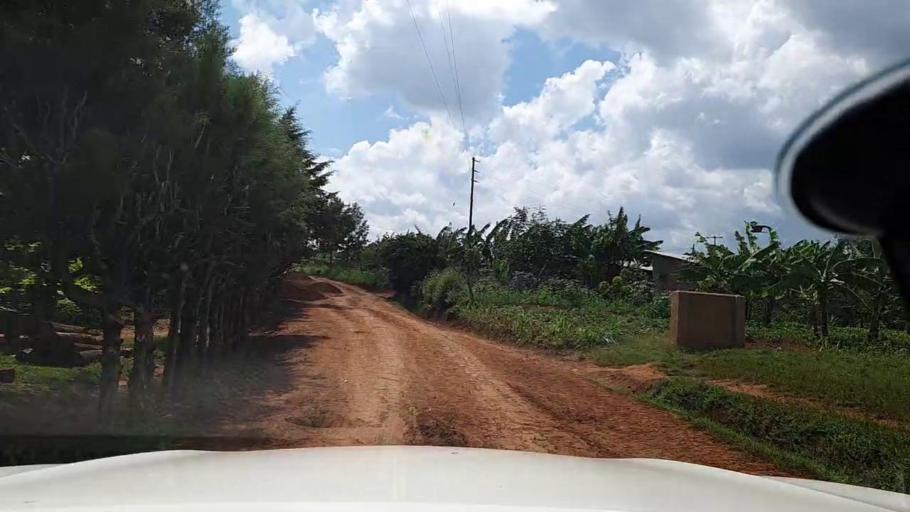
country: RW
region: Kigali
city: Kigali
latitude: -1.8330
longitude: 29.8375
